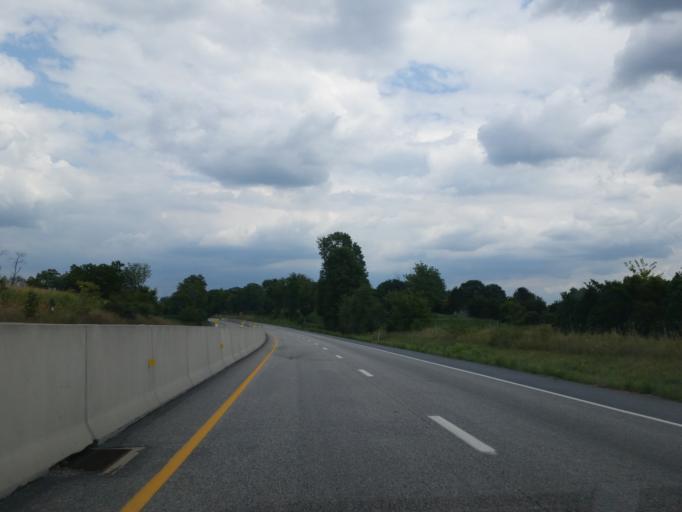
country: US
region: Pennsylvania
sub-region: Lebanon County
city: Jonestown
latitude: 40.4064
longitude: -76.5302
